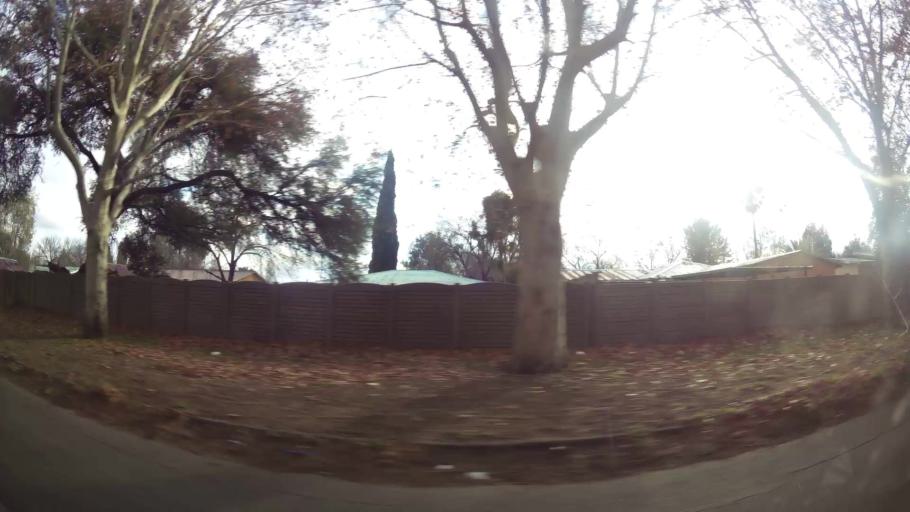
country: ZA
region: Orange Free State
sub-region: Fezile Dabi District Municipality
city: Sasolburg
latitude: -26.8255
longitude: 27.8239
